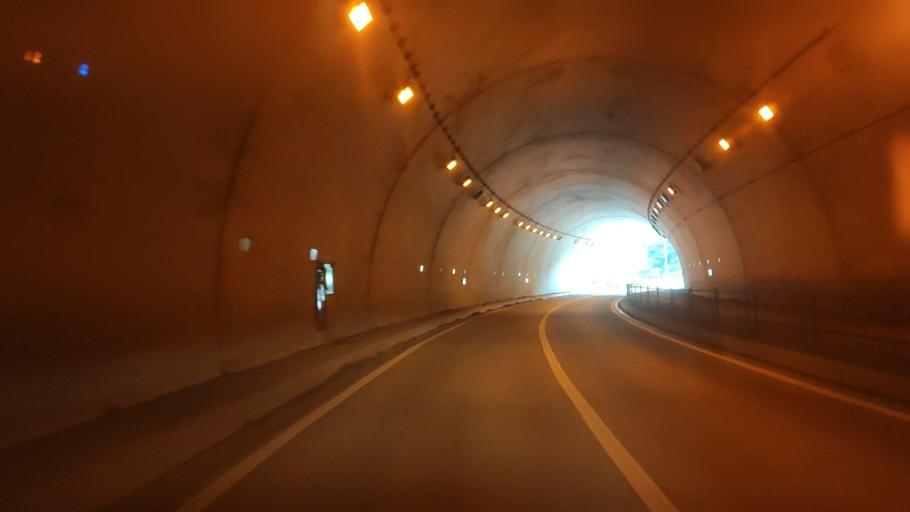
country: JP
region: Kumamoto
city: Hitoyoshi
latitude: 32.3874
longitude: 130.8349
